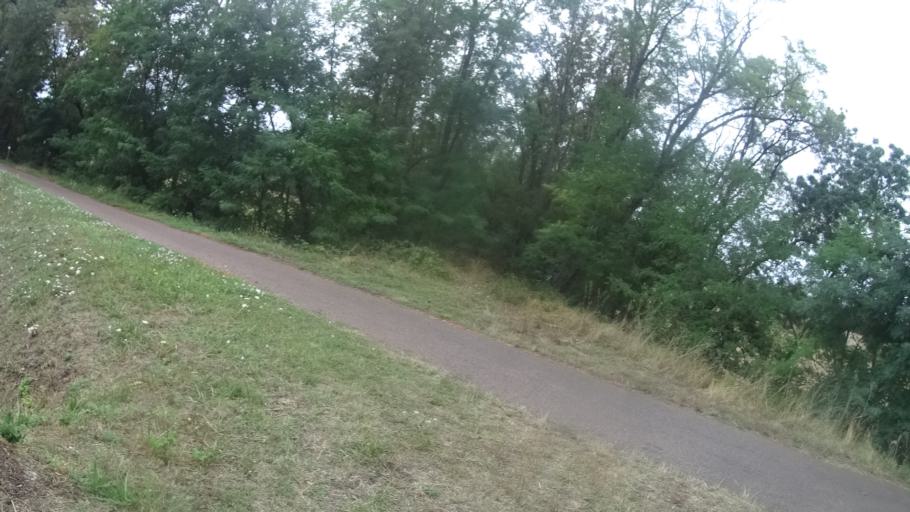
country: FR
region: Bourgogne
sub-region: Departement de la Nievre
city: Saint-Leger-des-Vignes
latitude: 46.8198
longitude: 3.4243
